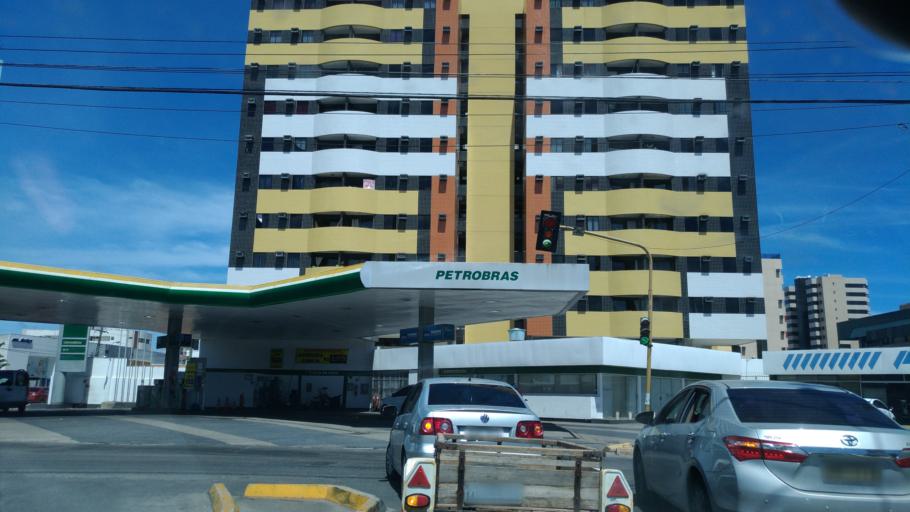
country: BR
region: Alagoas
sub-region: Maceio
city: Maceio
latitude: -9.6570
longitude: -35.7104
